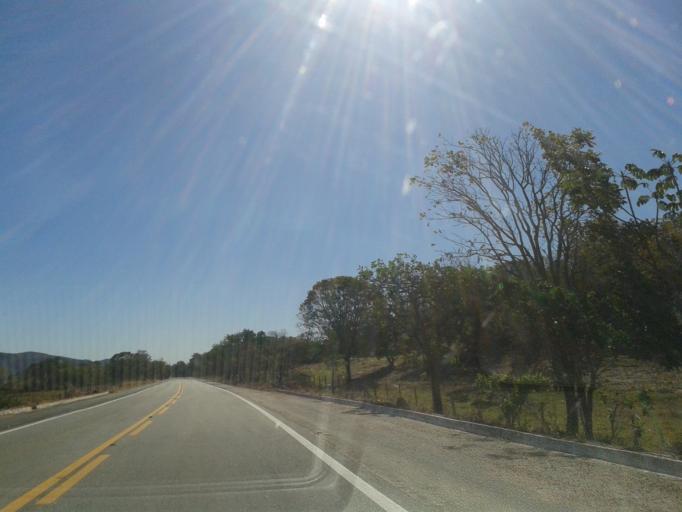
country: BR
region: Goias
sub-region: Goias
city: Goias
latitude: -15.8503
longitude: -50.0944
